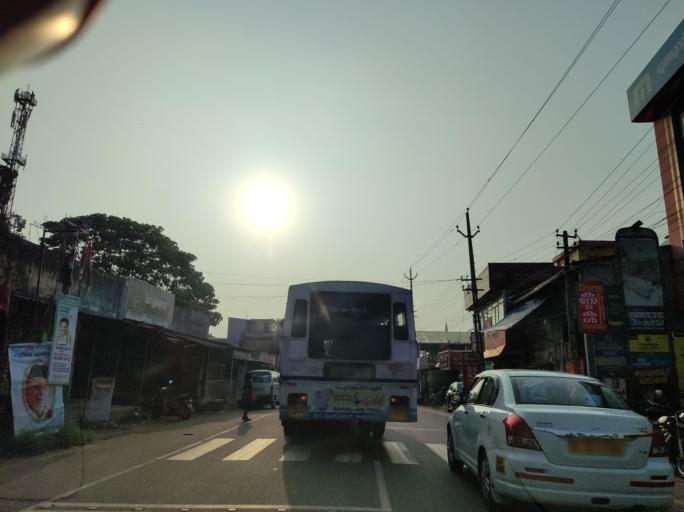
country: IN
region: Kerala
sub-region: Pattanamtitta
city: Adur
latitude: 9.1667
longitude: 76.6647
